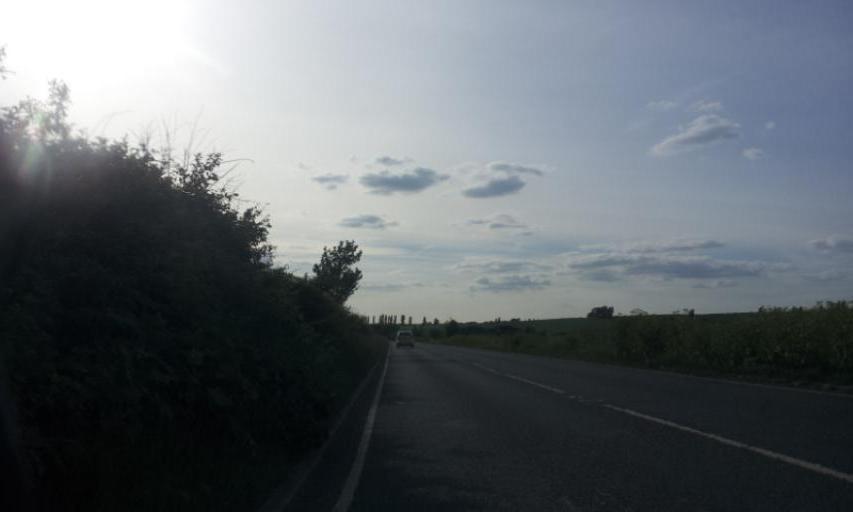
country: GB
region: England
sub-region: Kent
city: Leysdown-on-Sea
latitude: 51.3987
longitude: 0.8826
